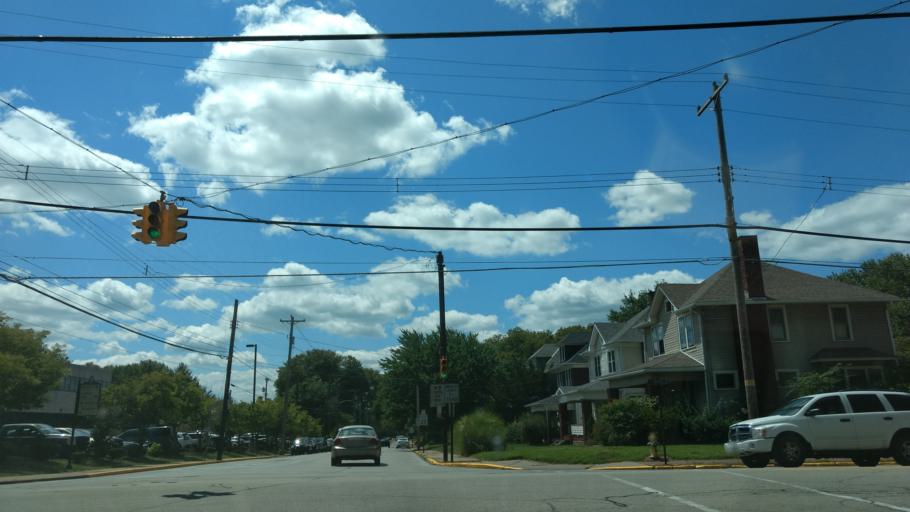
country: US
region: Pennsylvania
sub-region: Beaver County
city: Beaver
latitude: 40.6961
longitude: -80.3084
